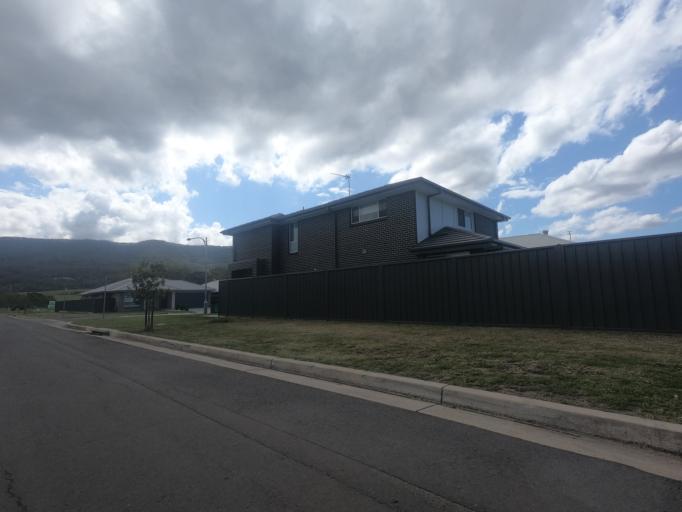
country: AU
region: New South Wales
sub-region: Wollongong
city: Dapto
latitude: -34.4894
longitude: 150.7650
